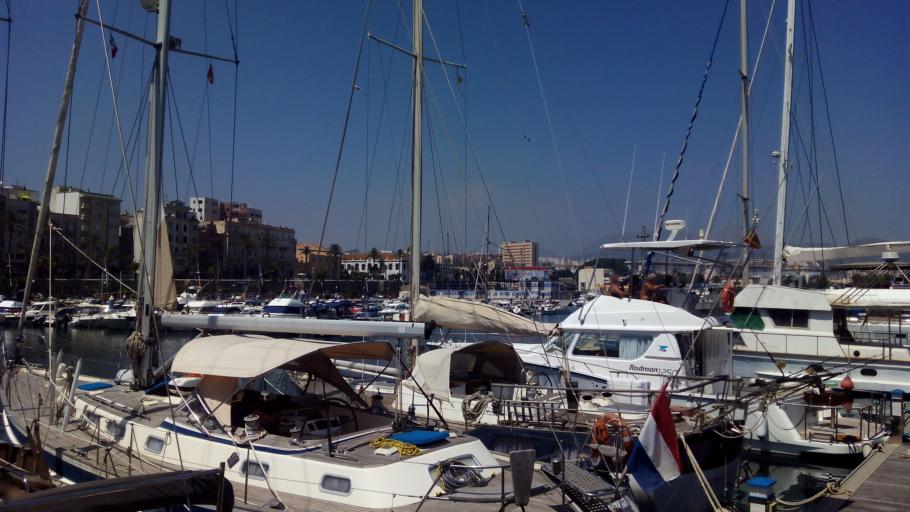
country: ES
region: Ceuta
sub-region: Ceuta
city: Ceuta
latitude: 35.8902
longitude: -5.3134
